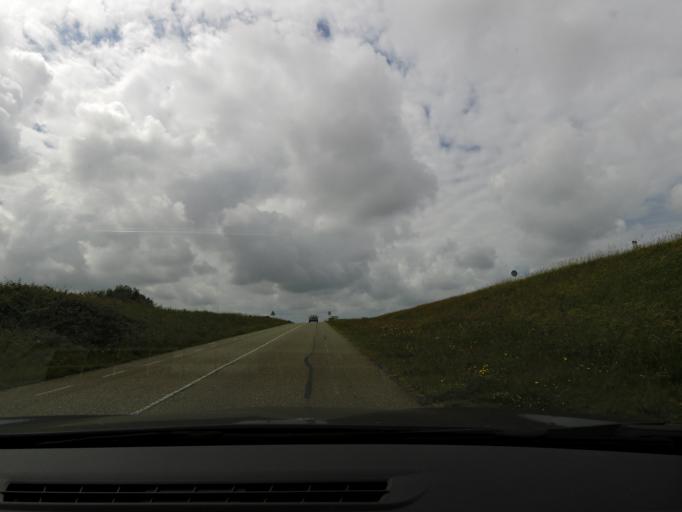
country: NL
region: Zeeland
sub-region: Gemeente Veere
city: Veere
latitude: 51.5892
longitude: 3.6624
